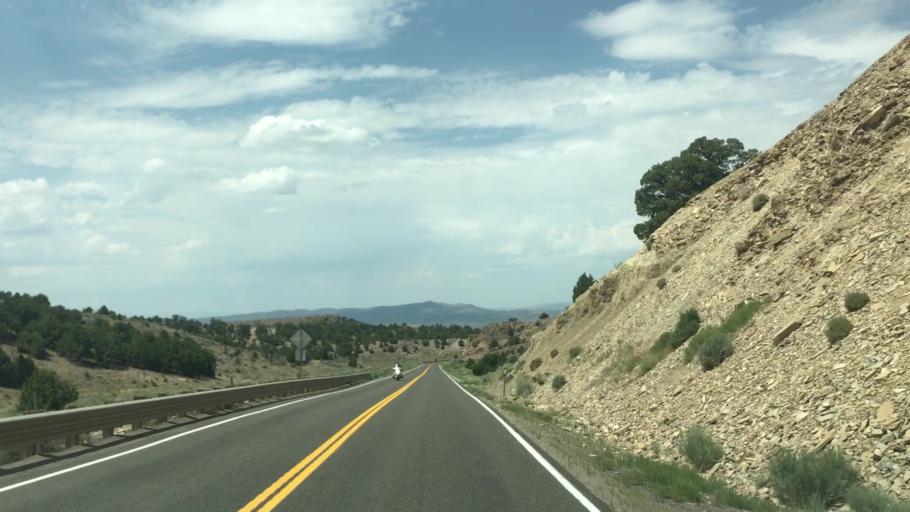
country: US
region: Nevada
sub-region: Eureka County
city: Eureka
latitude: 39.3916
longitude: -115.4967
